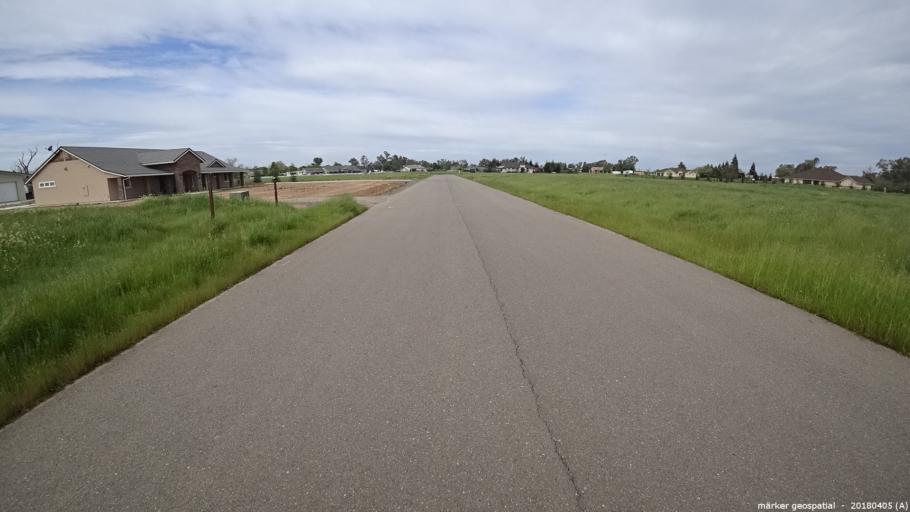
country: US
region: California
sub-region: Sacramento County
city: Galt
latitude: 38.2662
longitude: -121.3322
